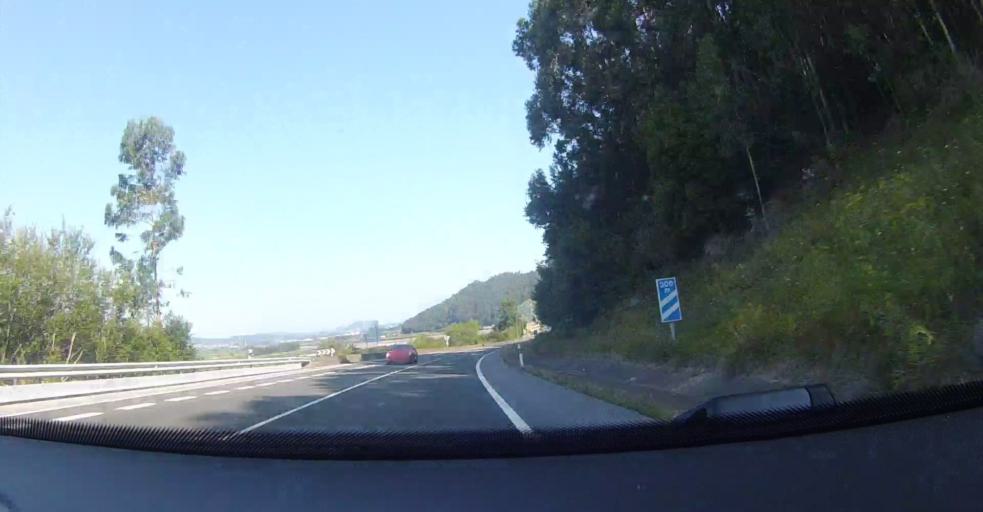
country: ES
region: Cantabria
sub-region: Provincia de Cantabria
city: Limpias
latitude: 43.3694
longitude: -3.4269
